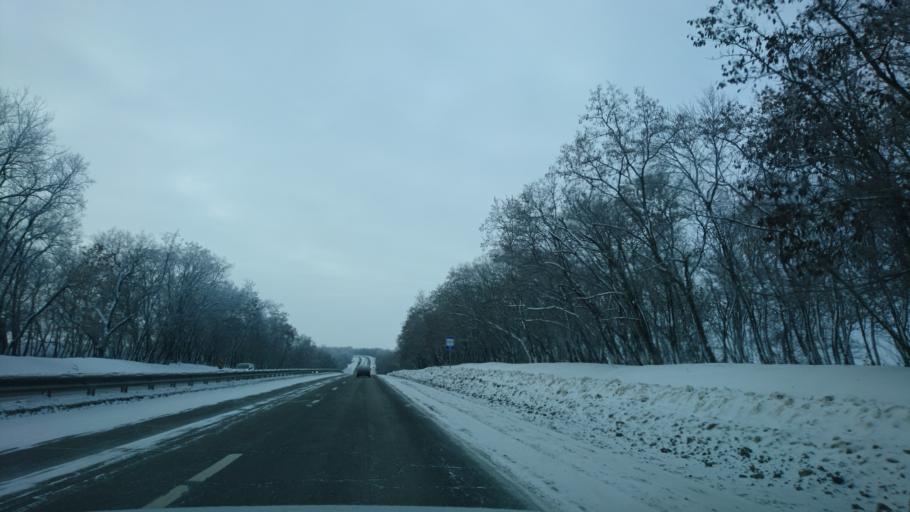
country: RU
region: Belgorod
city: Mayskiy
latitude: 50.4900
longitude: 36.4180
